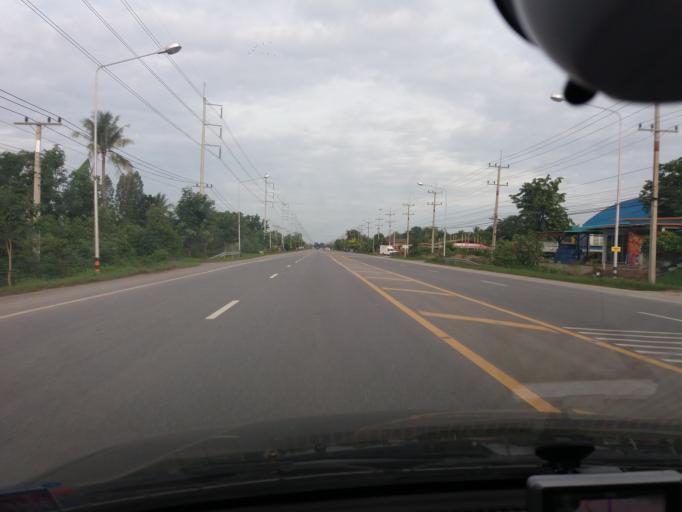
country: TH
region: Kanchanaburi
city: Huai Krachao
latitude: 14.3348
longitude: 99.7811
